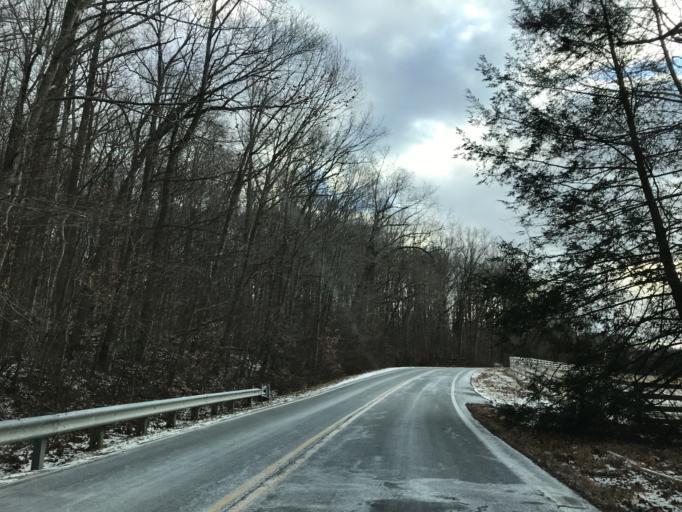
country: US
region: Maryland
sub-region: Harford County
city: Bel Air North
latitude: 39.6279
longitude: -76.3748
